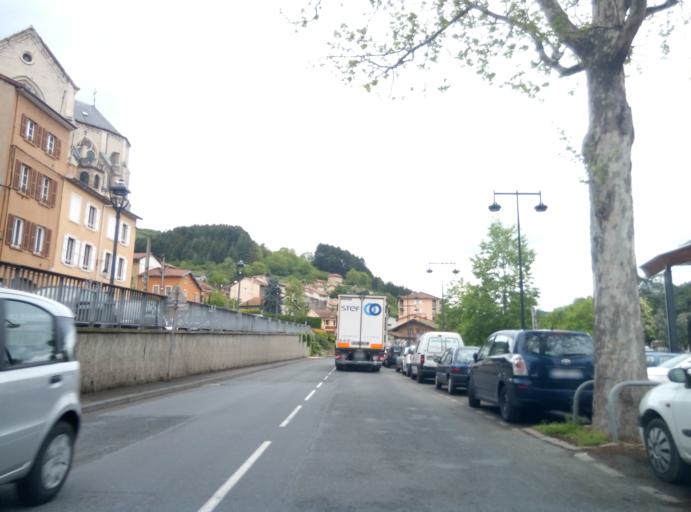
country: FR
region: Rhone-Alpes
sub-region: Departement du Rhone
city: Tarare
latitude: 45.8971
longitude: 4.4326
